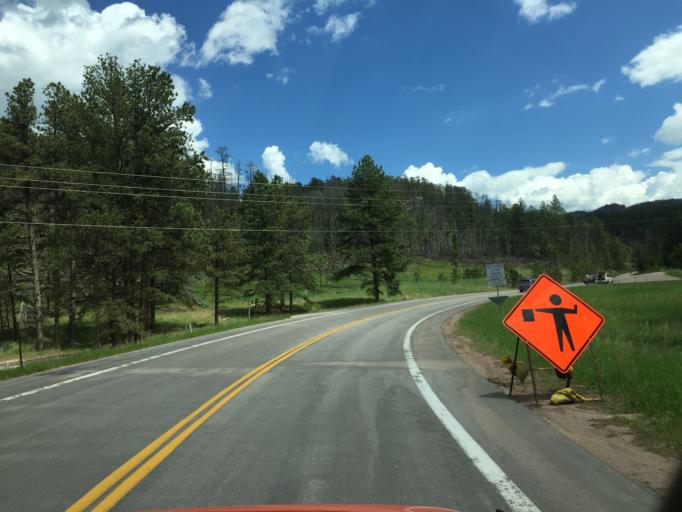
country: US
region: South Dakota
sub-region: Custer County
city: Custer
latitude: 43.8896
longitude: -103.5868
